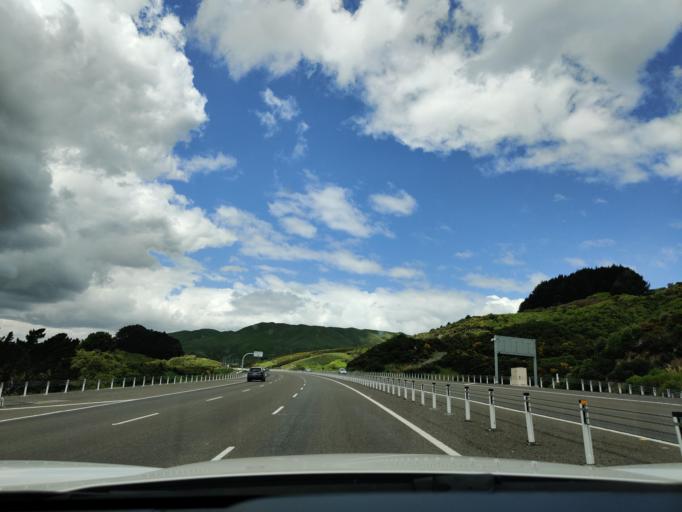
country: NZ
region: Wellington
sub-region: Porirua City
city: Porirua
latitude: -41.1533
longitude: 174.8602
